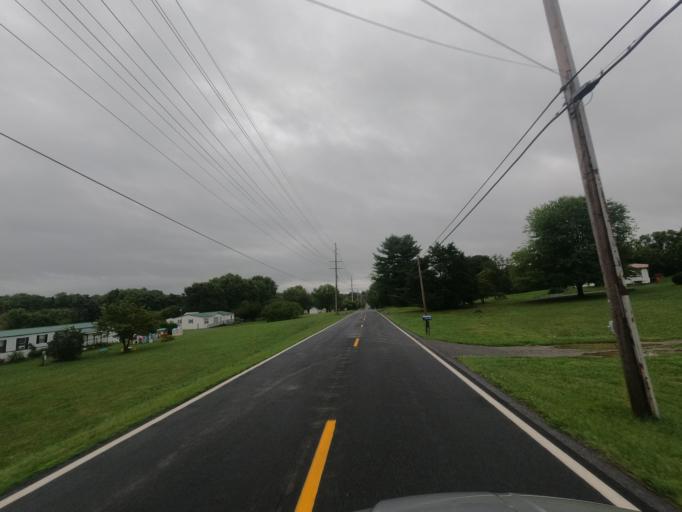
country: US
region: Maryland
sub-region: Washington County
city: Wilson-Conococheague
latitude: 39.6243
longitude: -77.9604
